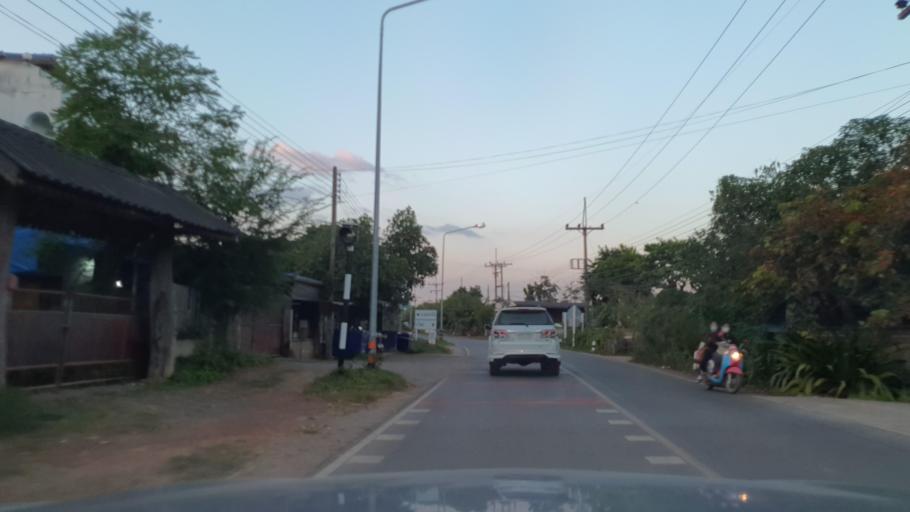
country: TH
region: Phayao
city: Dok Kham Tai
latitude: 19.0399
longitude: 100.0629
